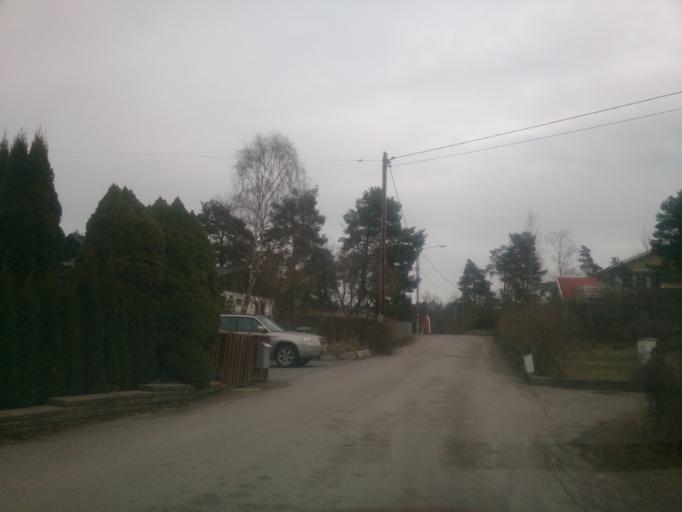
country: SE
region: OEstergoetland
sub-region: Norrkopings Kommun
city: Jursla
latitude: 58.6749
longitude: 16.1837
